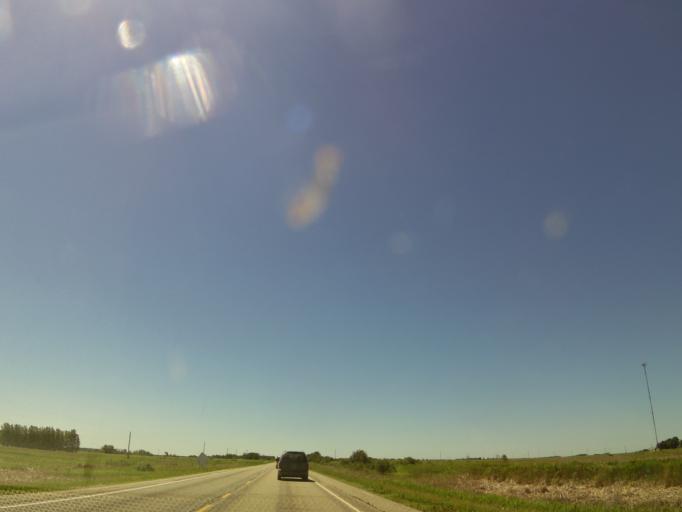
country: US
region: Minnesota
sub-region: Mahnomen County
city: Mahnomen
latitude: 47.3733
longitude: -95.9703
